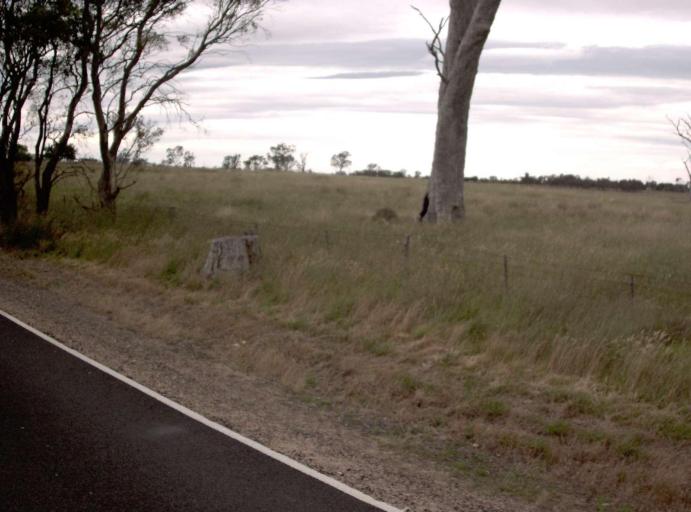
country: AU
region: Victoria
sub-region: Wellington
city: Sale
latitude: -38.0002
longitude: 147.1913
